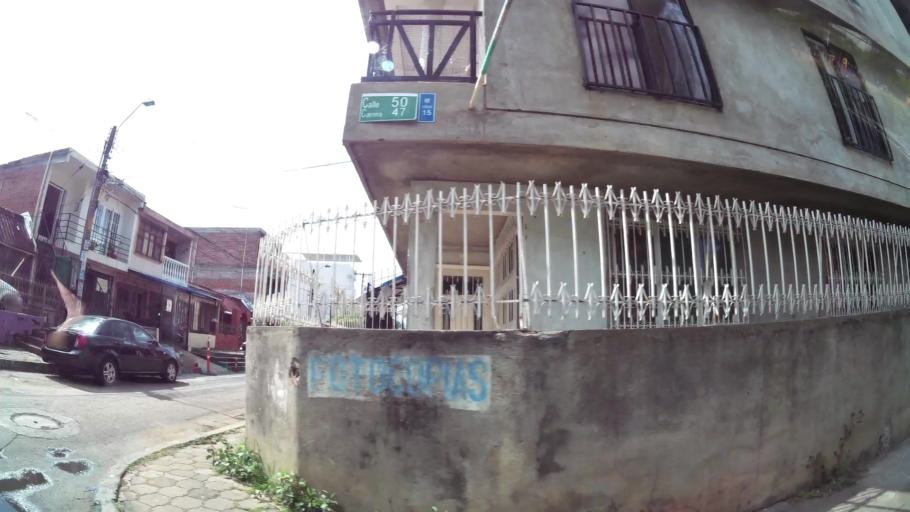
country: CO
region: Valle del Cauca
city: Cali
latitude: 3.3995
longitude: -76.5108
